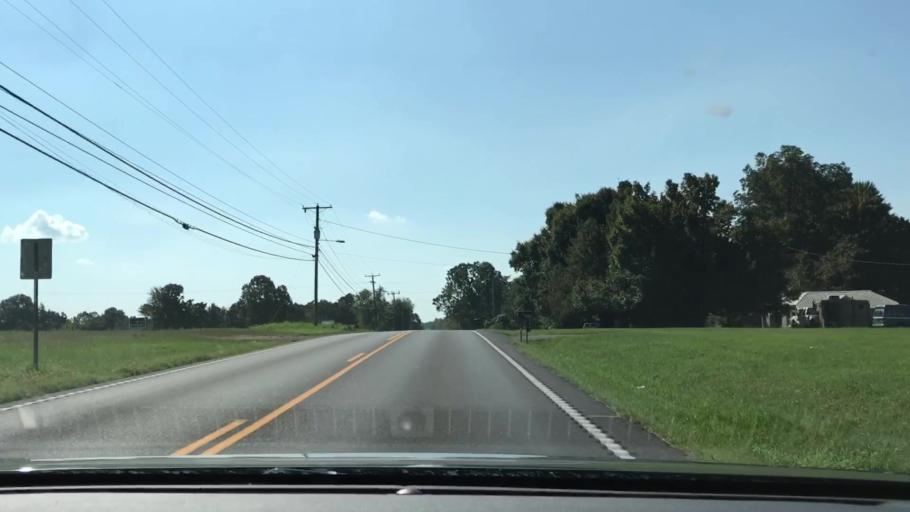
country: US
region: Kentucky
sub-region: Marshall County
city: Benton
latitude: 36.8299
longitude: -88.3506
